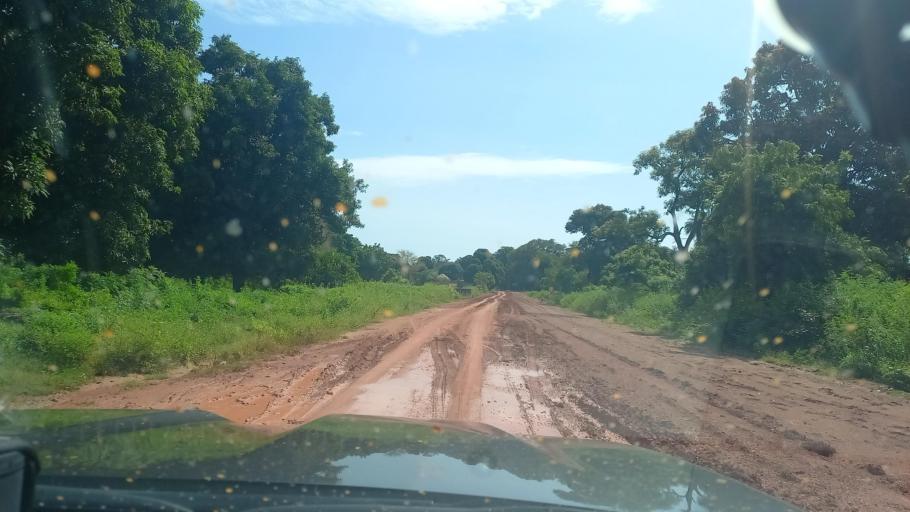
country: SN
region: Ziguinchor
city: Adeane
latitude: 12.6689
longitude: -16.0939
